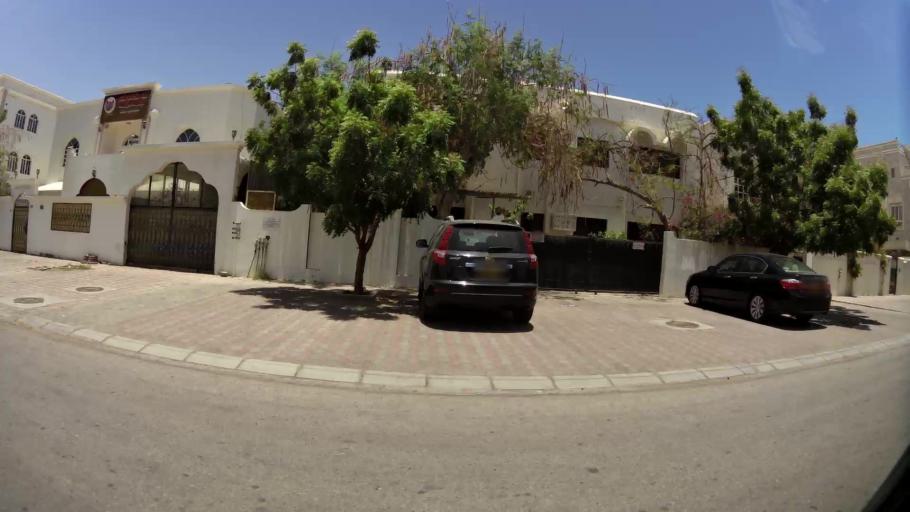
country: OM
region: Muhafazat Masqat
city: Bawshar
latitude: 23.6015
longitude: 58.4067
